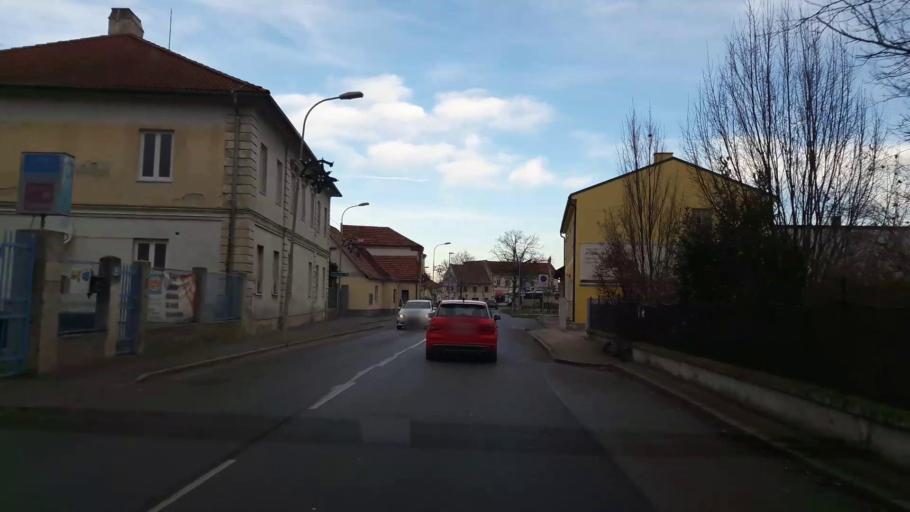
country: AT
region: Lower Austria
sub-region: Politischer Bezirk Baden
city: Ebreichsdorf
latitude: 47.9600
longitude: 16.4294
